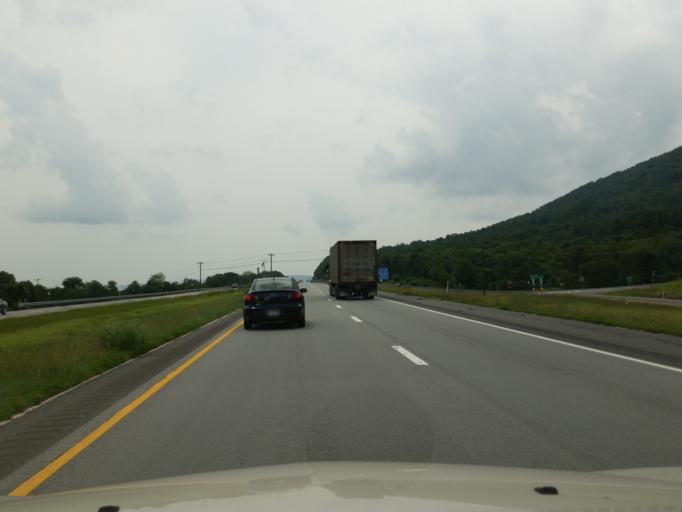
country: US
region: Pennsylvania
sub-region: Perry County
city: Newport
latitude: 40.4946
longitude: -77.1054
